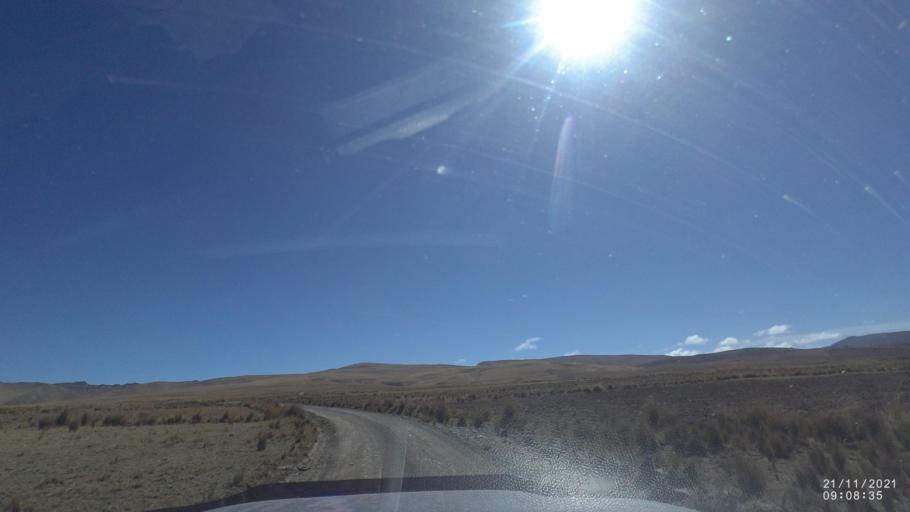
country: BO
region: Cochabamba
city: Cochabamba
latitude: -17.1617
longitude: -66.2670
